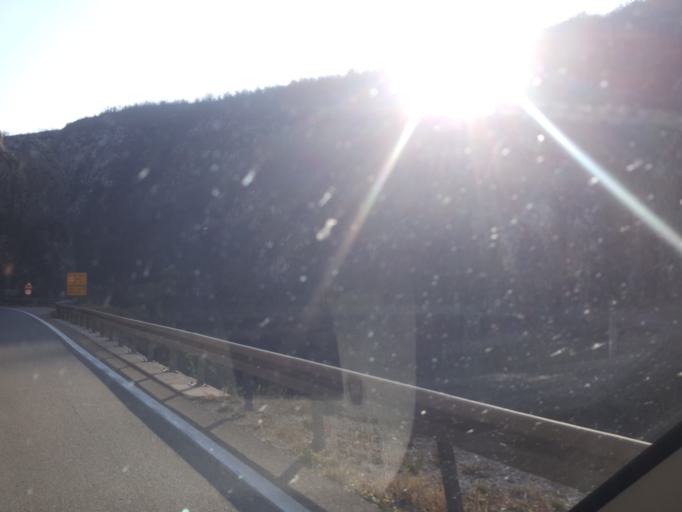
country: RS
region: Central Serbia
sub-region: Nisavski Okrug
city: Svrljig
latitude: 43.3144
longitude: 22.1770
